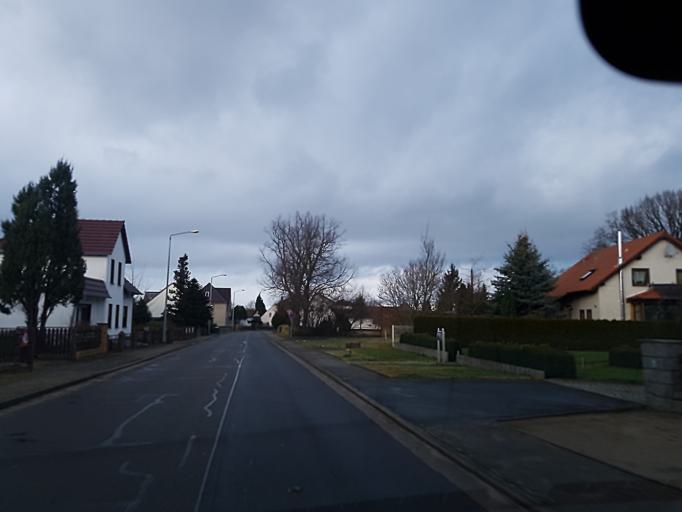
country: DE
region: Brandenburg
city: Elsterwerda
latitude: 51.4912
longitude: 13.5065
